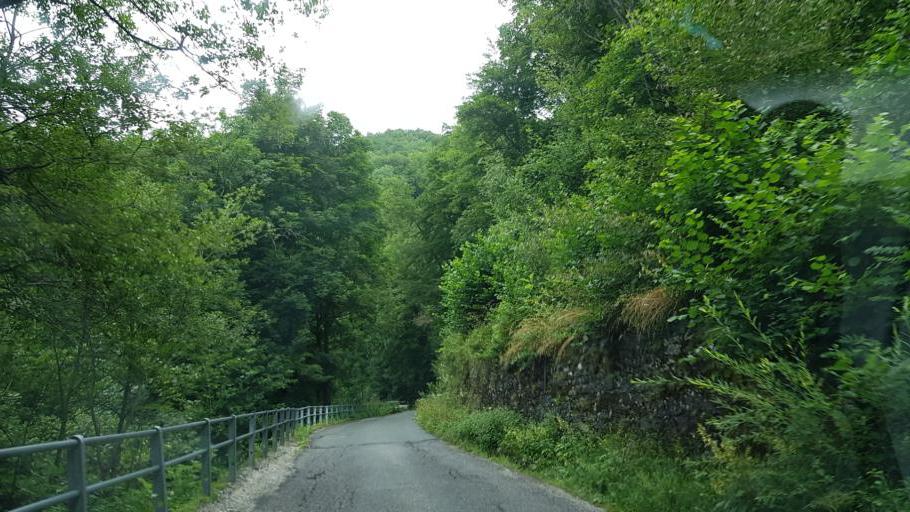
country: IT
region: Piedmont
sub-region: Provincia di Cuneo
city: Stroppo
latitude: 44.5202
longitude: 7.1286
